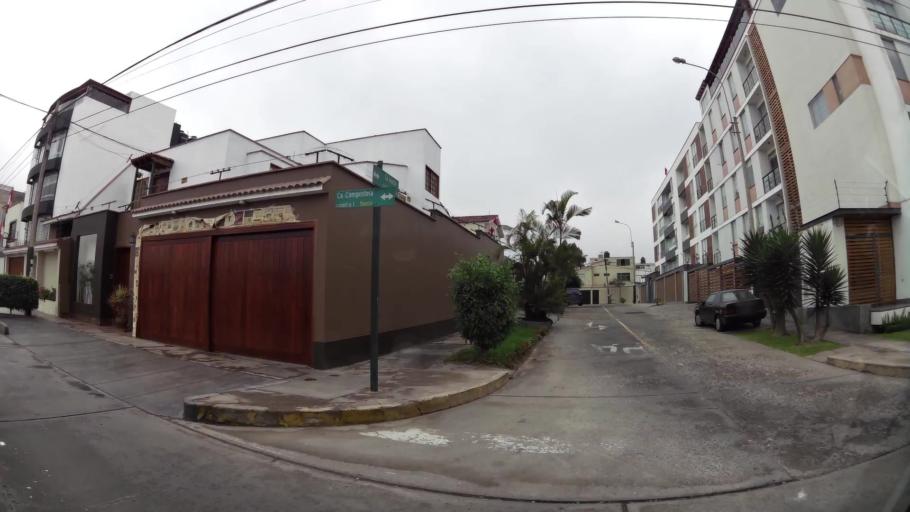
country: PE
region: Lima
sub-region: Lima
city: Surco
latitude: -12.1341
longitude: -77.0014
